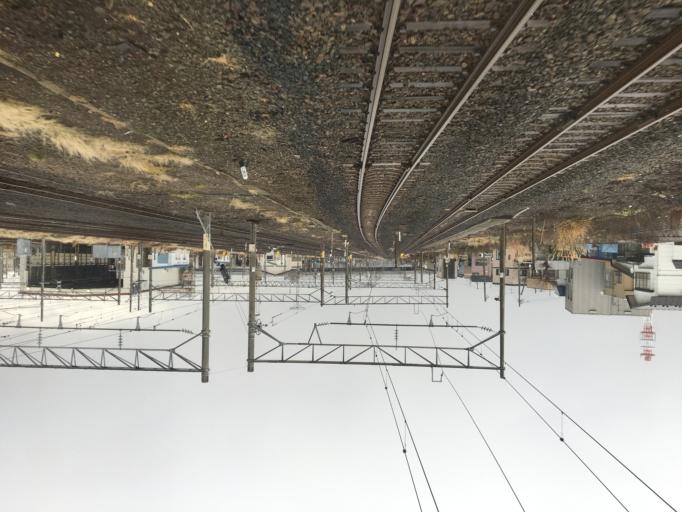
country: JP
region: Aomori
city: Aomori Shi
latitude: 40.8185
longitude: 140.7392
